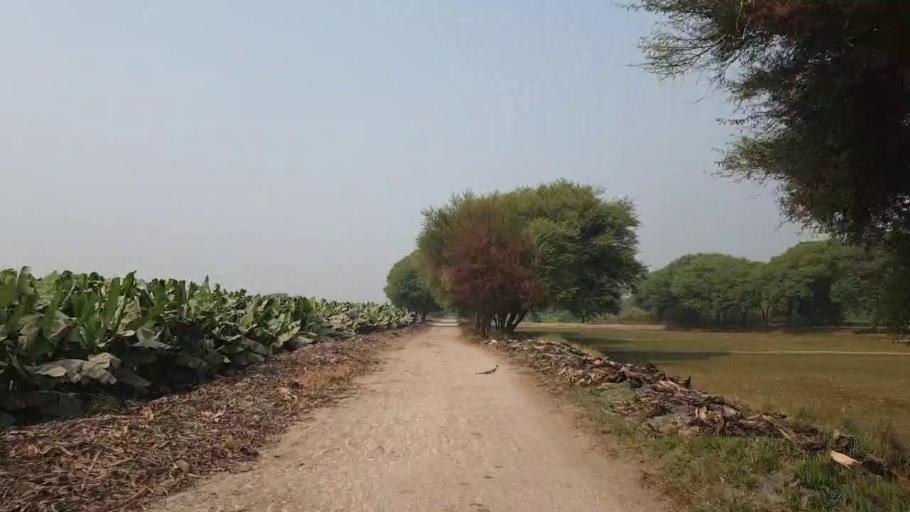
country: PK
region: Sindh
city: Tando Muhammad Khan
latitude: 25.2133
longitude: 68.5570
